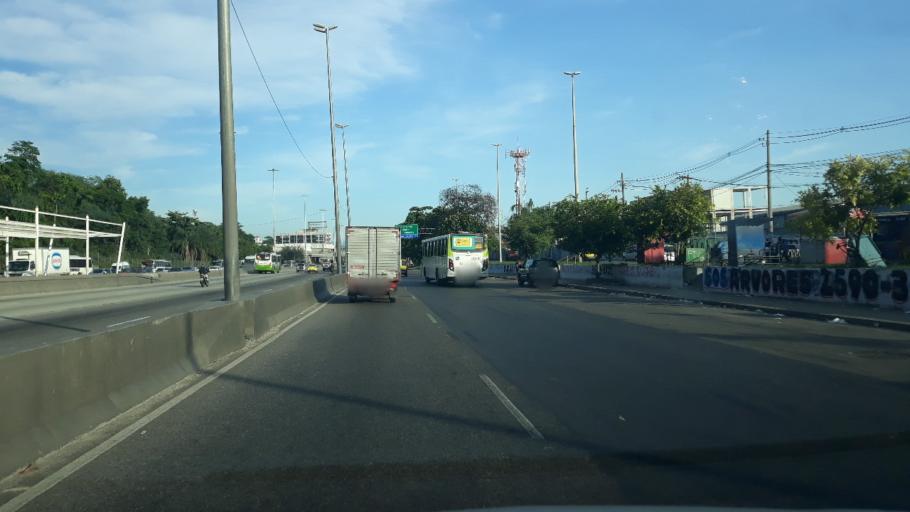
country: BR
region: Rio de Janeiro
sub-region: Rio De Janeiro
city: Rio de Janeiro
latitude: -22.8748
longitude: -43.2432
